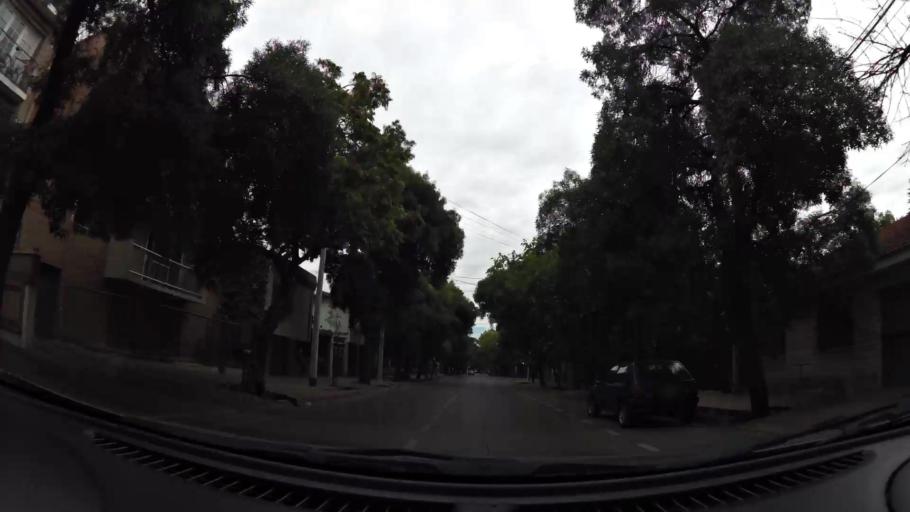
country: AR
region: Mendoza
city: Mendoza
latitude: -32.8886
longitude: -68.8590
